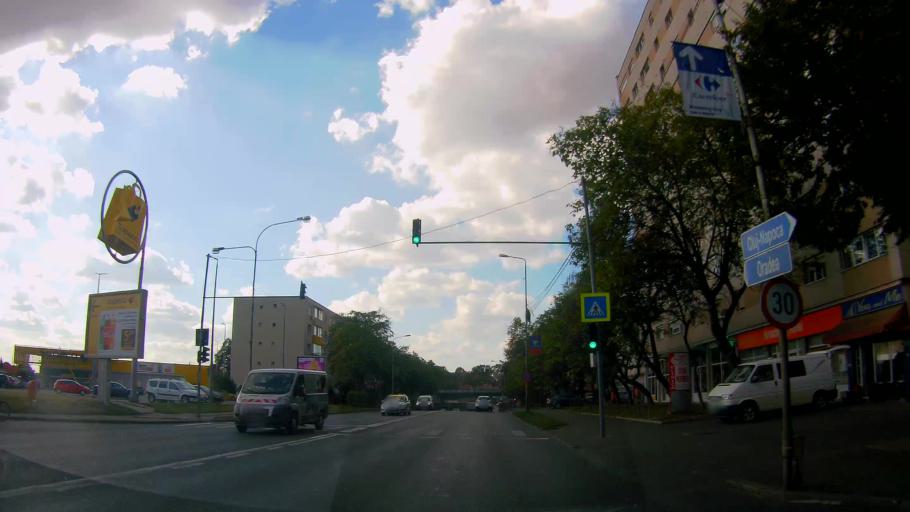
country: RO
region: Satu Mare
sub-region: Municipiul Satu Mare
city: Satu Mare
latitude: 47.7805
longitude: 22.8809
